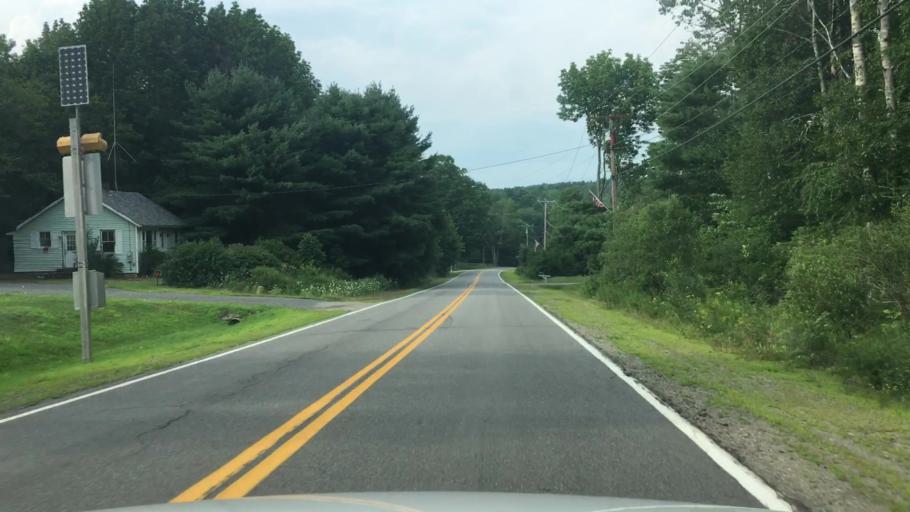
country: US
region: Maine
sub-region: Knox County
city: Washington
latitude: 44.2691
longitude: -69.3717
